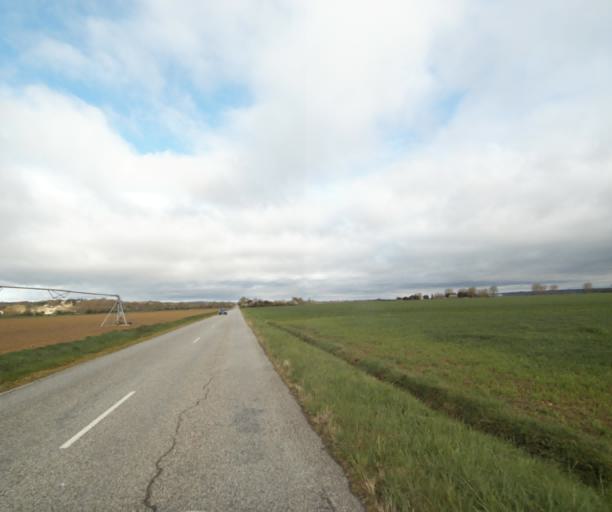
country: FR
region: Midi-Pyrenees
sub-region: Departement de l'Ariege
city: Saverdun
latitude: 43.2527
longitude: 1.5465
